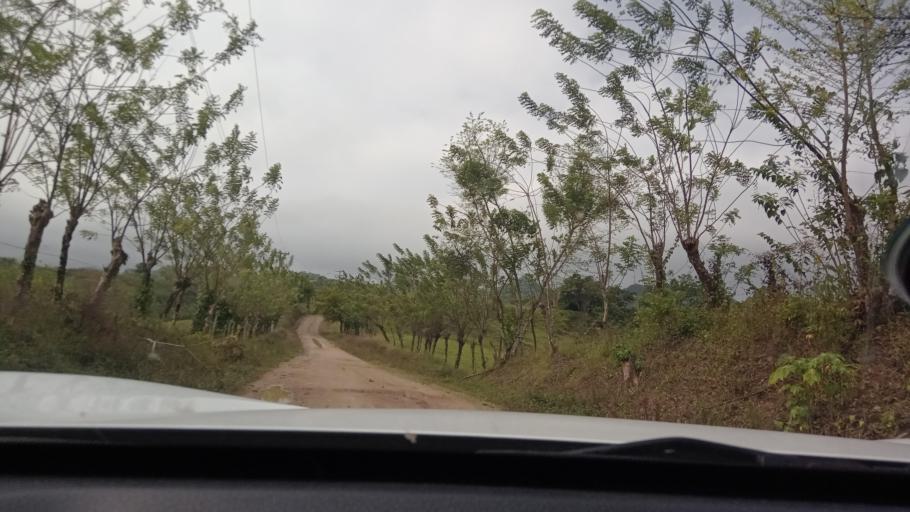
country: MX
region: Tabasco
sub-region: Huimanguillo
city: Francisco Rueda
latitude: 17.5132
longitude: -94.1186
